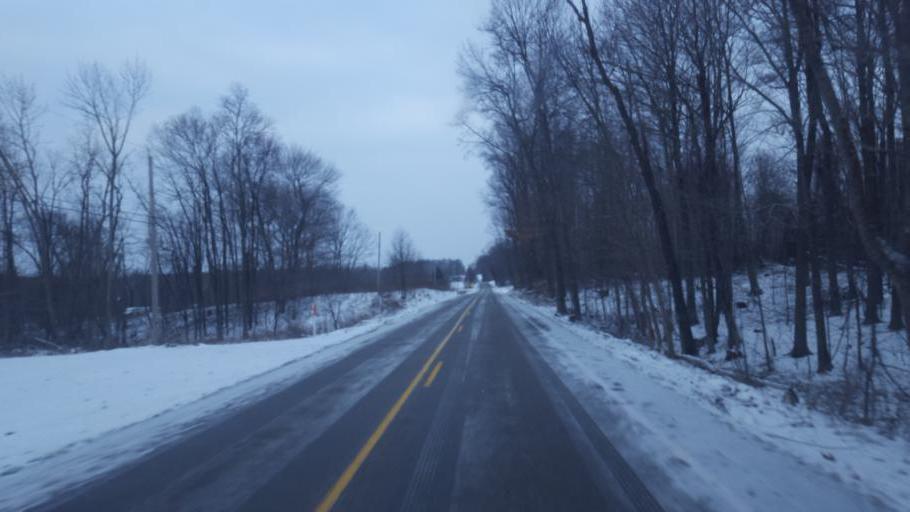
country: US
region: Pennsylvania
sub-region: Mercer County
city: Stoneboro
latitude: 41.4040
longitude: -80.0043
